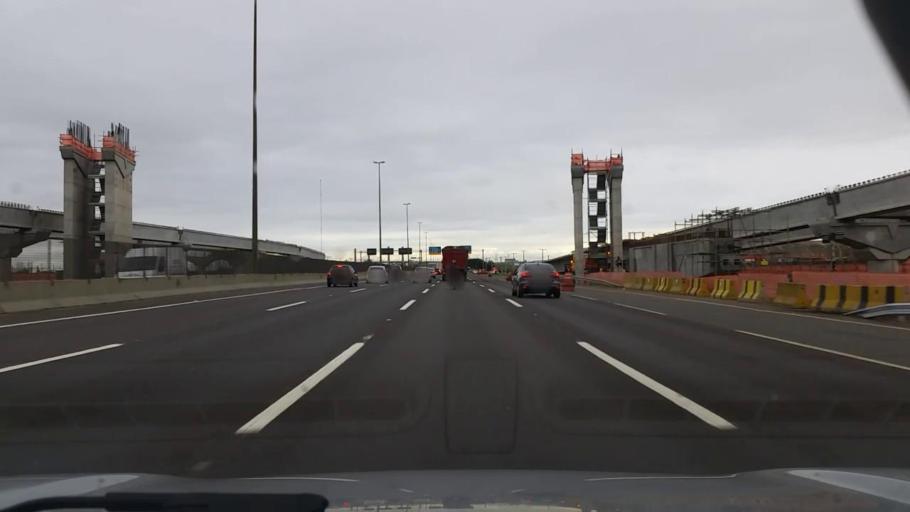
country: BR
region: Rio Grande do Sul
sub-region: Porto Alegre
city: Porto Alegre
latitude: -29.9872
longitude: -51.2029
